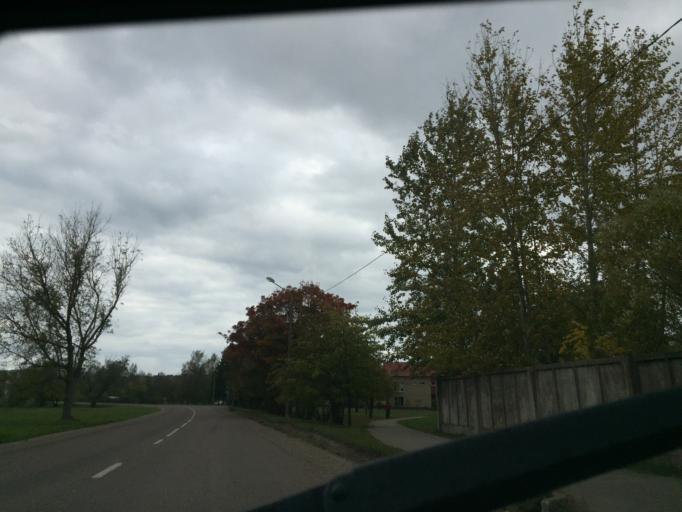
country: LV
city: Tireli
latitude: 56.7970
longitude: 23.6144
